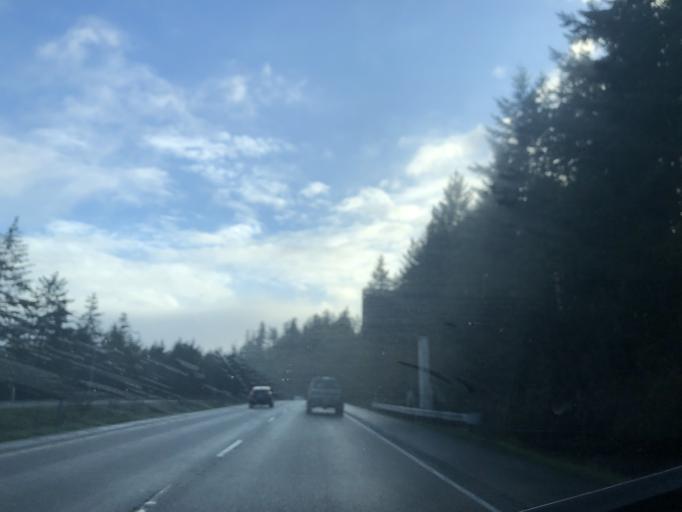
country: US
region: Washington
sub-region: Kitsap County
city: Erlands Point-Kitsap Lake
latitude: 47.5874
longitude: -122.6991
